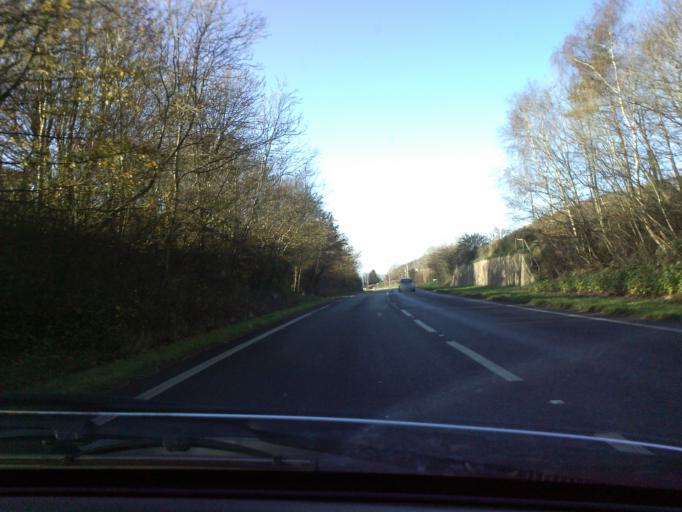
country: GB
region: England
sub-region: Dorset
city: Bridport
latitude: 50.7357
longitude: -2.7349
